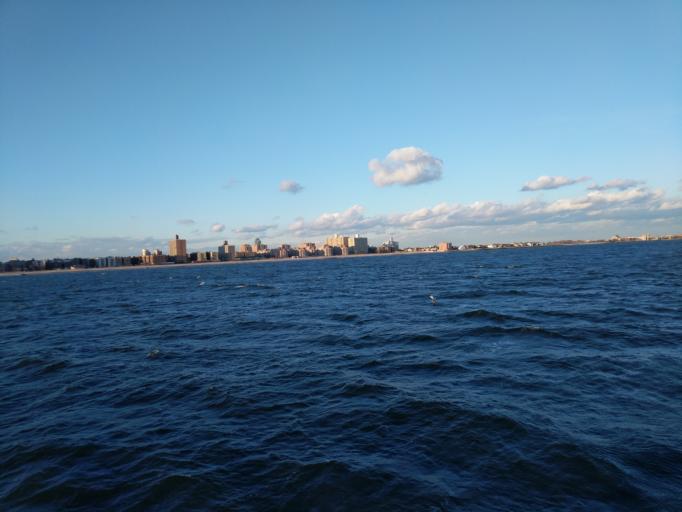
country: US
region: New York
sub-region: Kings County
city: Coney Island
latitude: 40.5654
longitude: -73.9658
